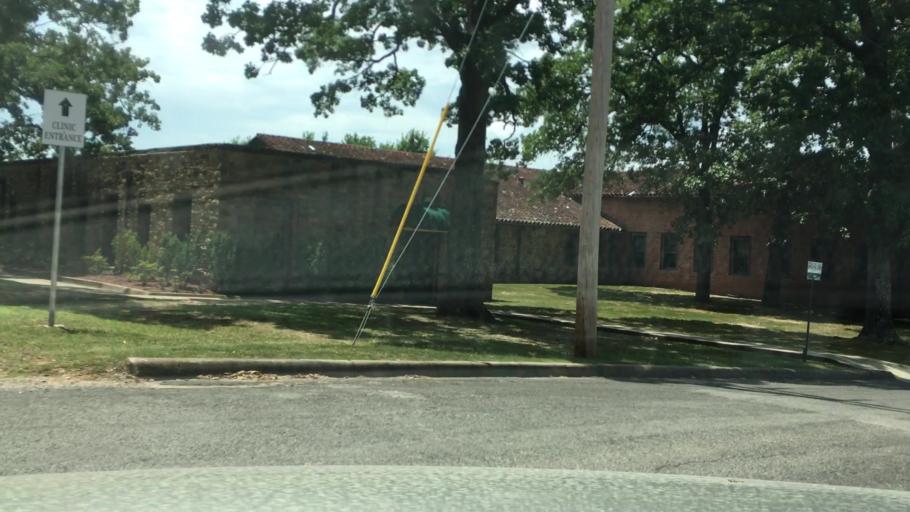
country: US
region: Oklahoma
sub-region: Cherokee County
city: Tahlequah
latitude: 35.9255
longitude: -94.9669
